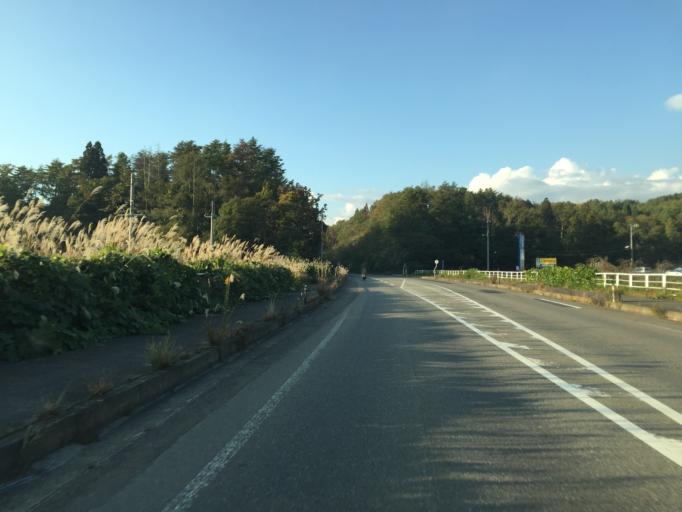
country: JP
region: Fukushima
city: Kitakata
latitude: 37.6919
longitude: 139.8901
